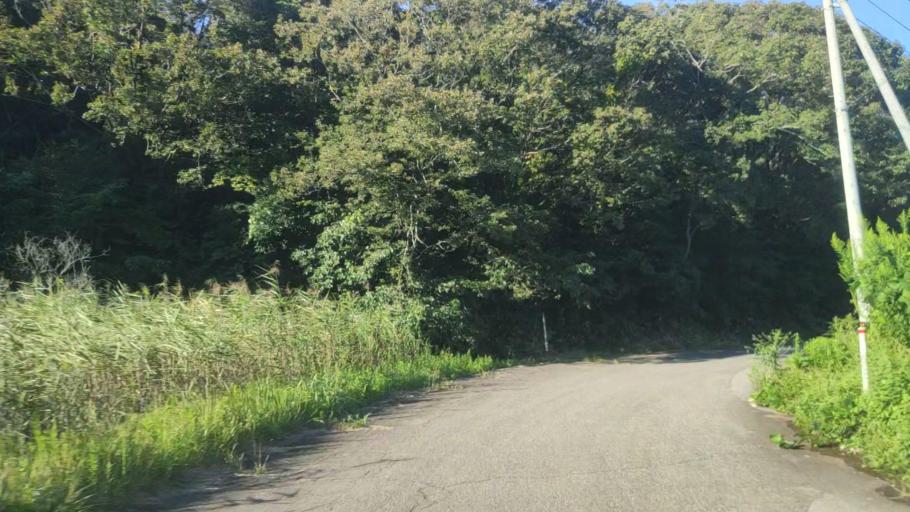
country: JP
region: Ishikawa
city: Nanao
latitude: 37.1239
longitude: 136.8947
